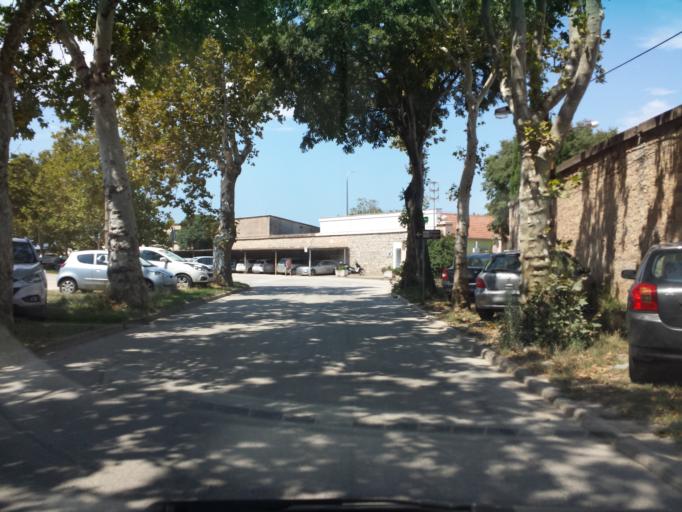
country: HR
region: Istarska
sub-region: Grad Pula
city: Pula
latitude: 44.8634
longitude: 13.8274
